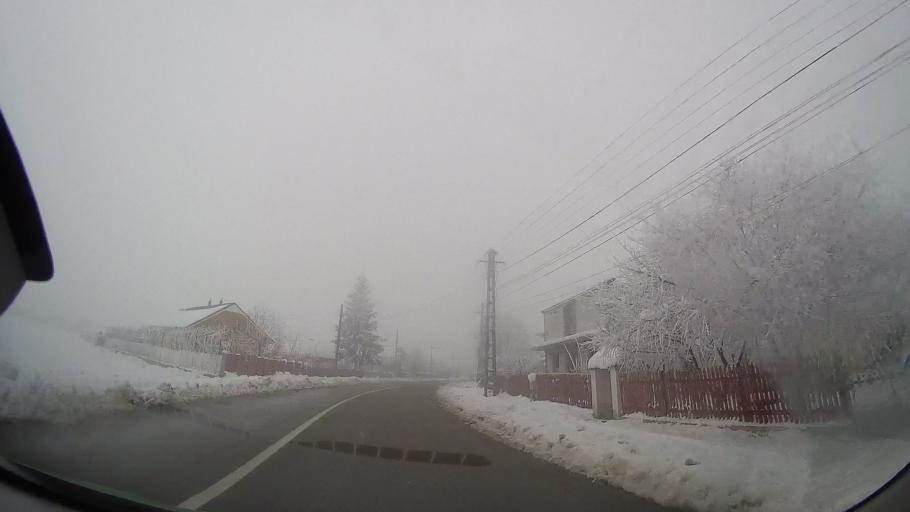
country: RO
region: Iasi
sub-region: Municipiul Pascani
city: Pascani
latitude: 47.2580
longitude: 26.7158
